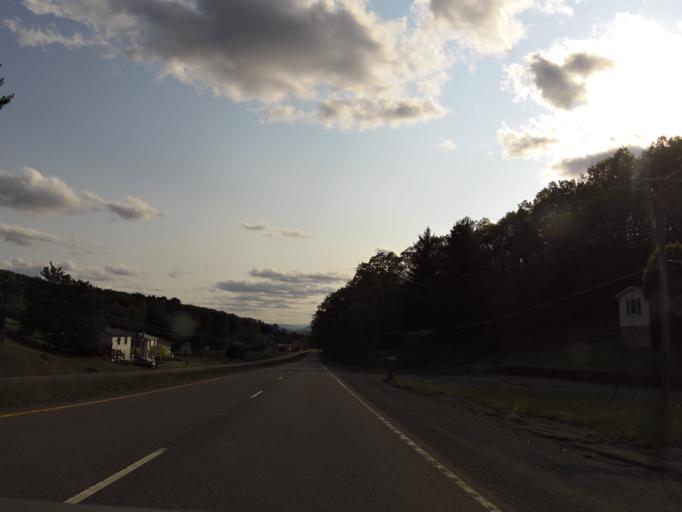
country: US
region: Virginia
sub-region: Tazewell County
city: Springville
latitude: 37.1806
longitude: -81.4328
